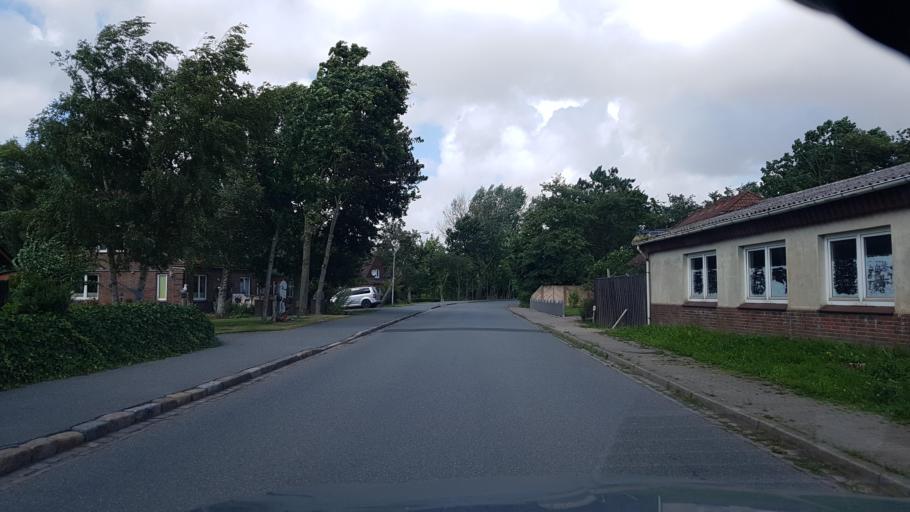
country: DE
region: Schleswig-Holstein
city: Suderdeich
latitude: 54.2034
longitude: 8.9119
